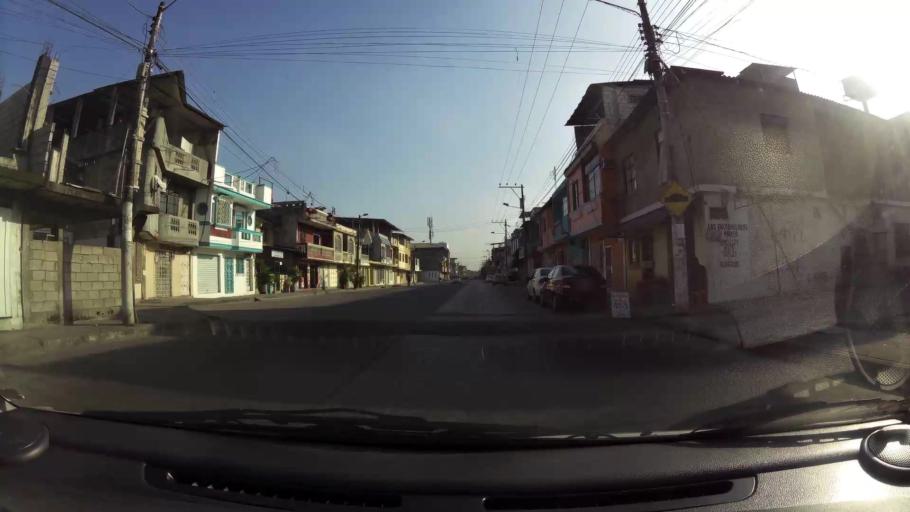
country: EC
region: Guayas
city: Eloy Alfaro
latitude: -2.1850
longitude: -79.8562
